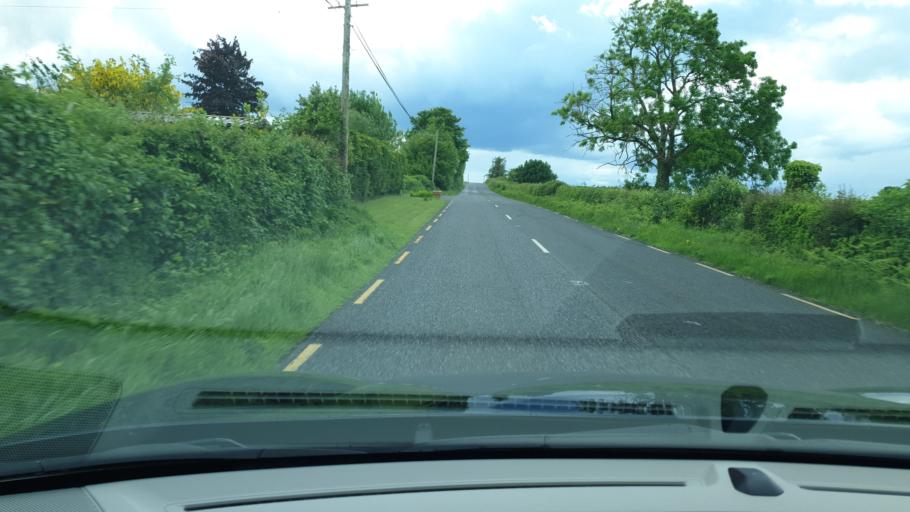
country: IE
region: Leinster
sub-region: Uibh Fhaili
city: Clara
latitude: 53.2336
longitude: -7.6218
